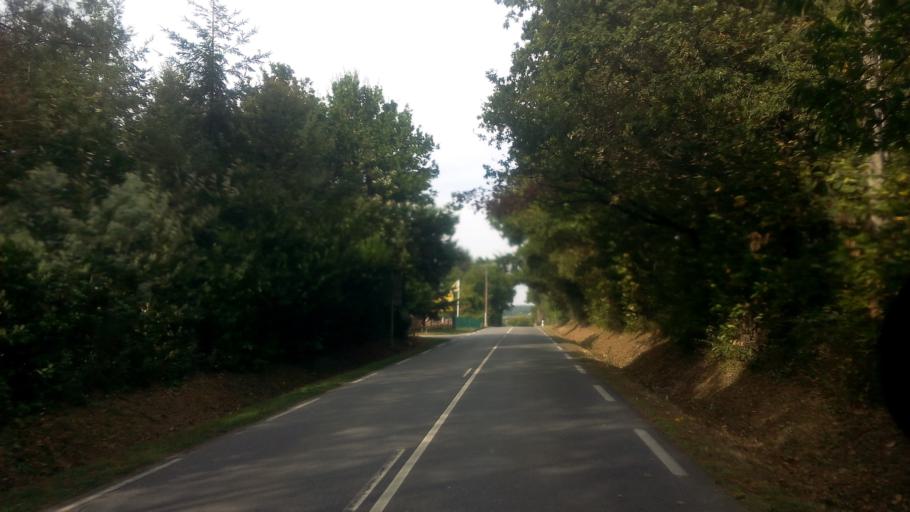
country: FR
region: Brittany
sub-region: Departement d'Ille-et-Vilaine
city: Bains-sur-Oust
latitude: 47.7237
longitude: -2.1016
